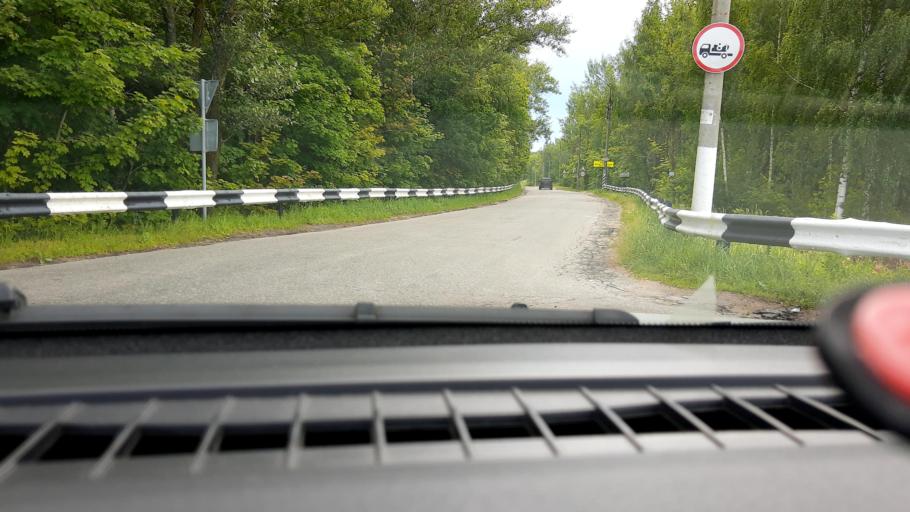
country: RU
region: Nizjnij Novgorod
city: Kstovo
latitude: 56.1468
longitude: 44.3295
